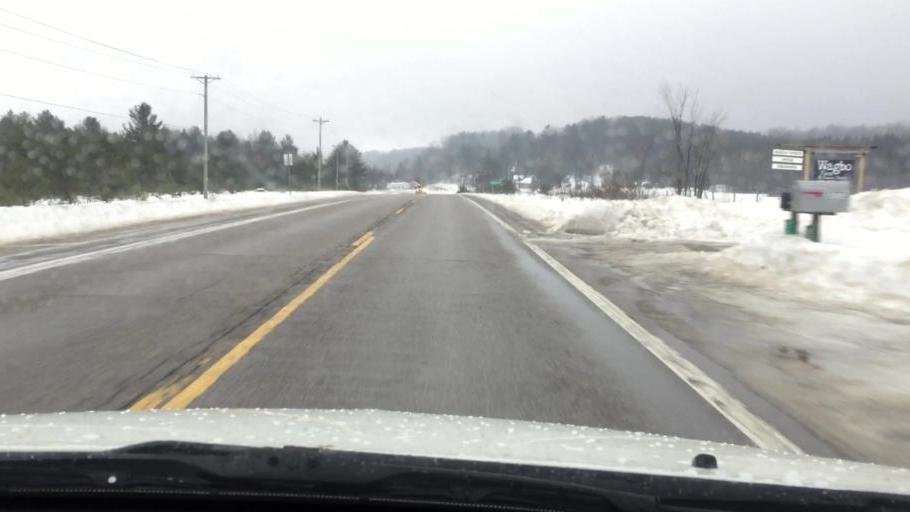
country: US
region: Michigan
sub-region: Charlevoix County
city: East Jordan
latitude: 45.1158
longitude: -85.1295
